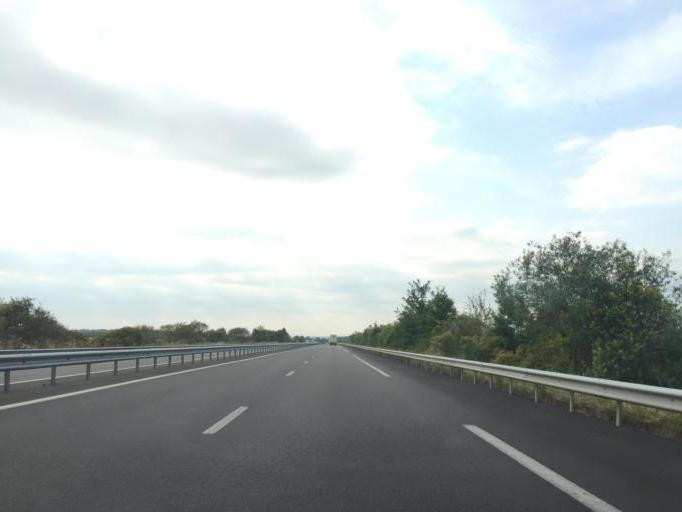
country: FR
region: Auvergne
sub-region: Departement de l'Allier
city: Saint-Francois
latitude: 46.4617
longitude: 3.8893
